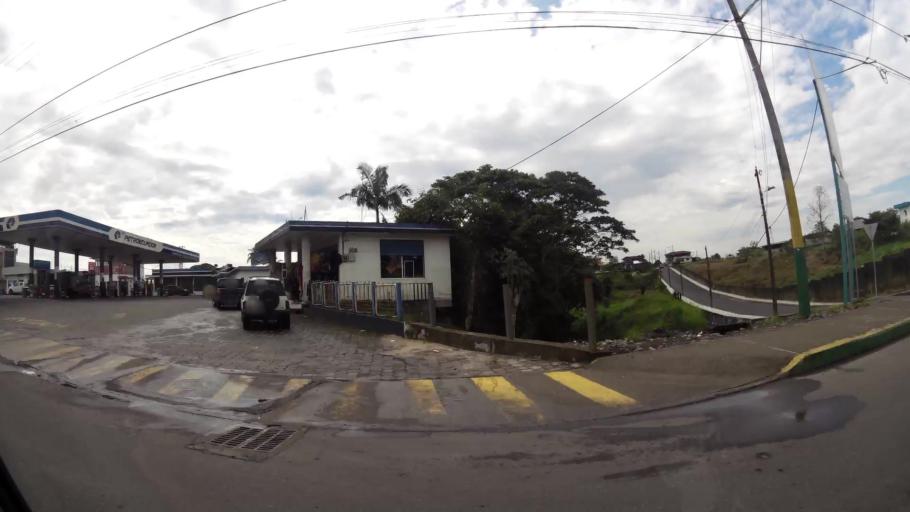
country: EC
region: Pastaza
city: Puyo
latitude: -1.4916
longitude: -77.9962
